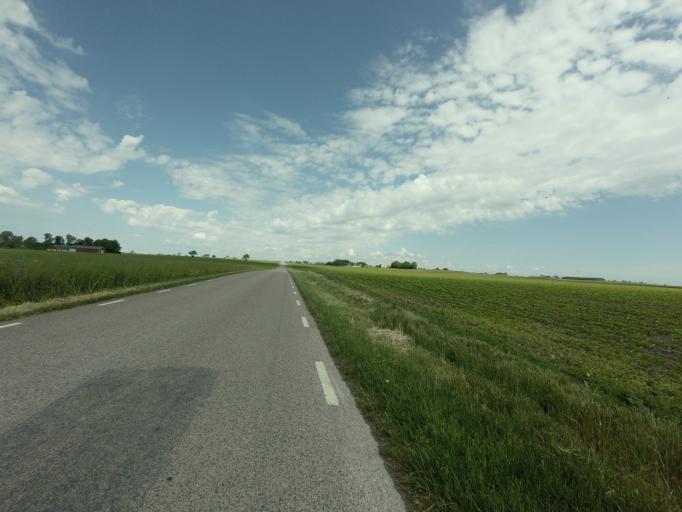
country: SE
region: Skane
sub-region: Trelleborgs Kommun
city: Skare
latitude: 55.4182
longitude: 13.1029
